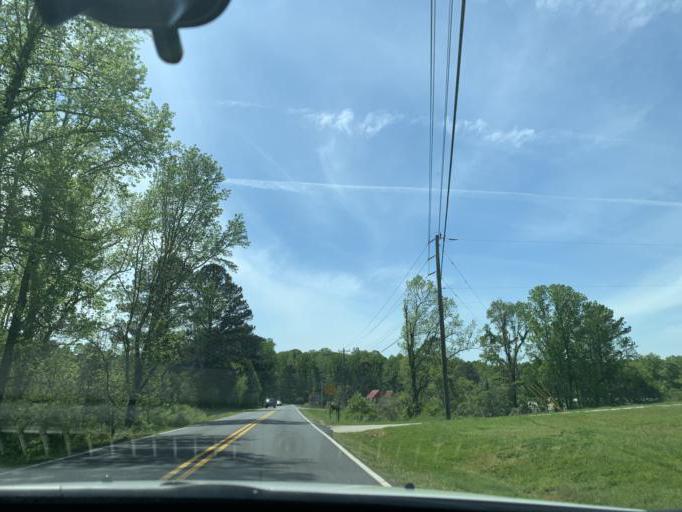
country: US
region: Georgia
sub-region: Forsyth County
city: Cumming
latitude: 34.2482
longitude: -84.1620
